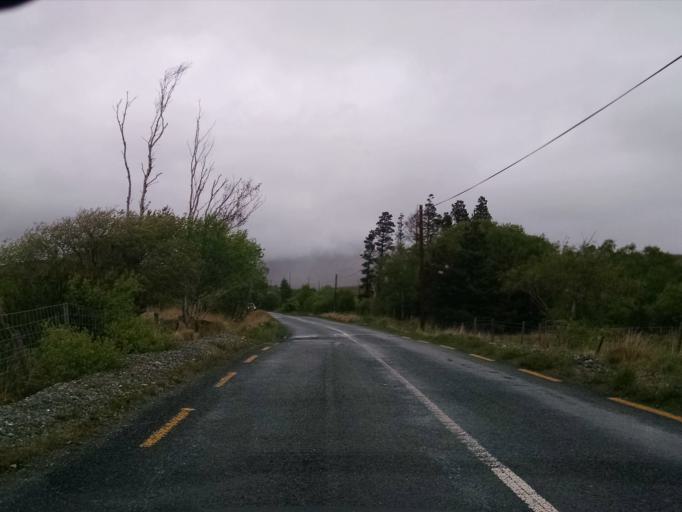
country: IE
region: Connaught
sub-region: County Galway
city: Clifden
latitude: 53.4857
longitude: -9.7399
